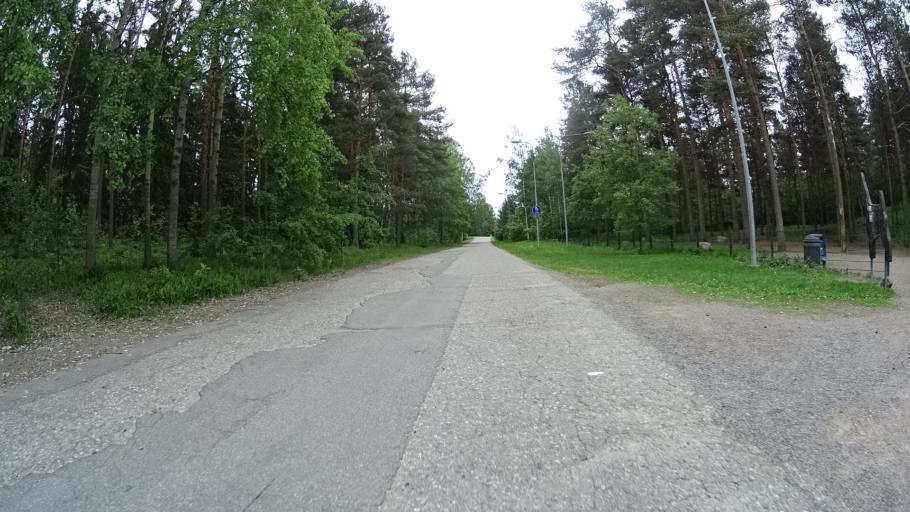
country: FI
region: Uusimaa
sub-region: Helsinki
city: Vantaa
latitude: 60.2646
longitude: 25.0672
